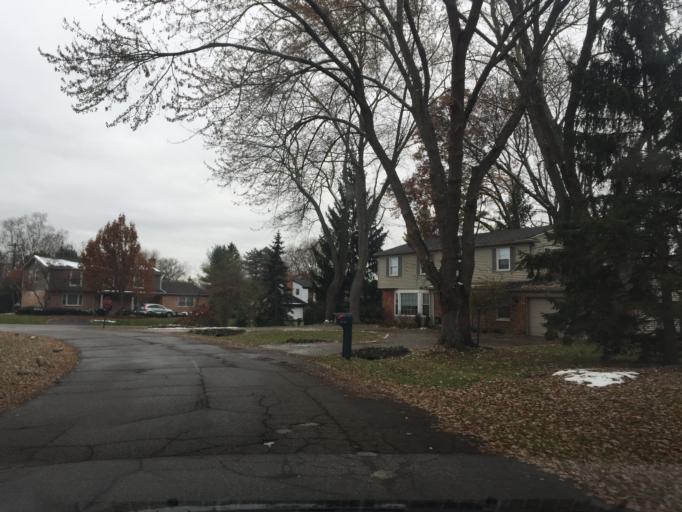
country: US
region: Michigan
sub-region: Oakland County
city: Franklin
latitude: 42.5356
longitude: -83.2901
